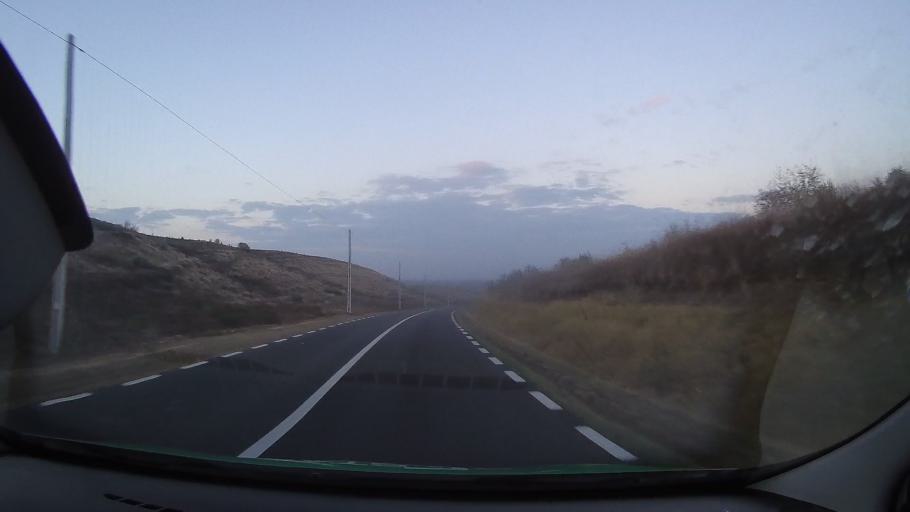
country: RO
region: Constanta
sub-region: Comuna Oltina
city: Oltina
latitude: 44.1387
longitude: 27.6653
